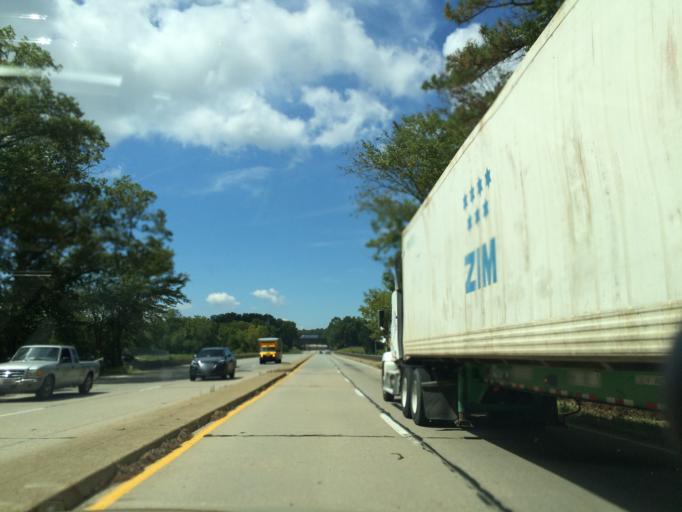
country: US
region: Virginia
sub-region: York County
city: Yorktown
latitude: 37.1728
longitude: -76.5603
